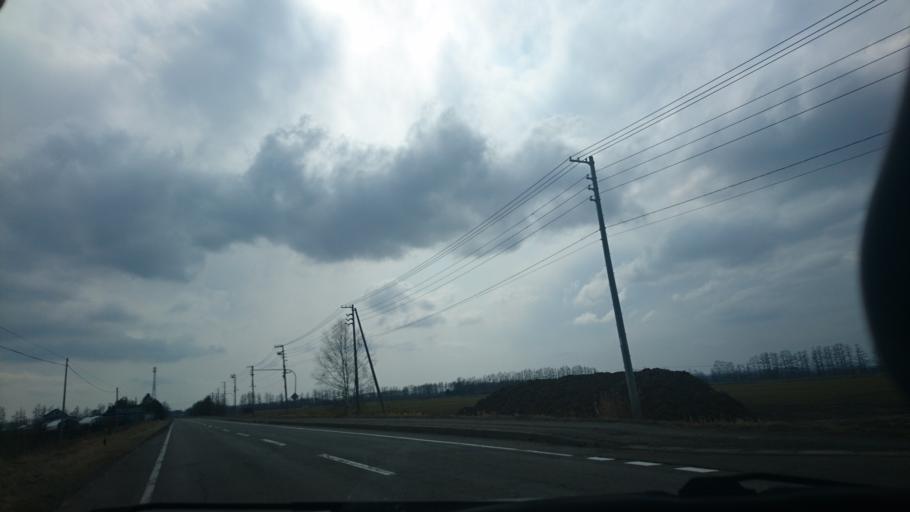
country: JP
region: Hokkaido
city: Otofuke
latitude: 43.2163
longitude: 143.2808
